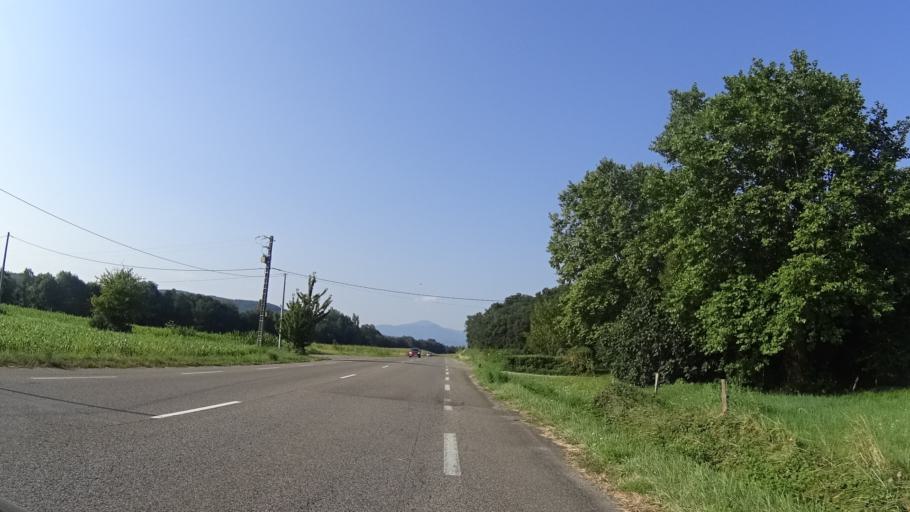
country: FR
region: Midi-Pyrenees
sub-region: Departement de l'Ariege
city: Mirepoix
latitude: 43.0234
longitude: 1.8936
